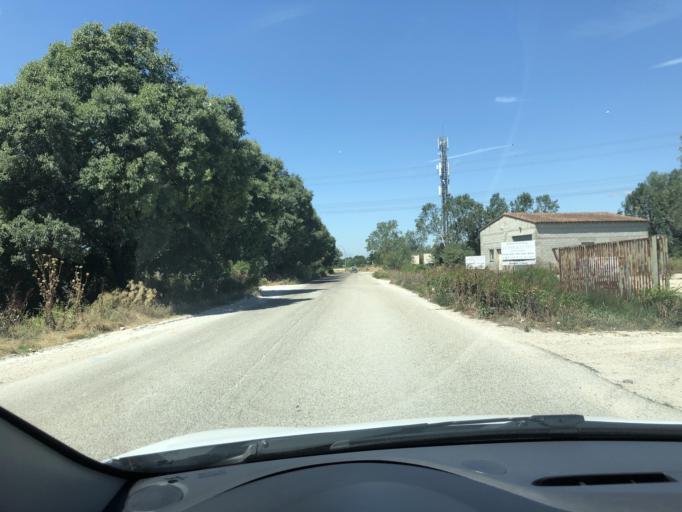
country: FR
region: Provence-Alpes-Cote d'Azur
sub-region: Departement des Bouches-du-Rhone
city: Chateaurenard
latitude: 43.9004
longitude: 4.8748
